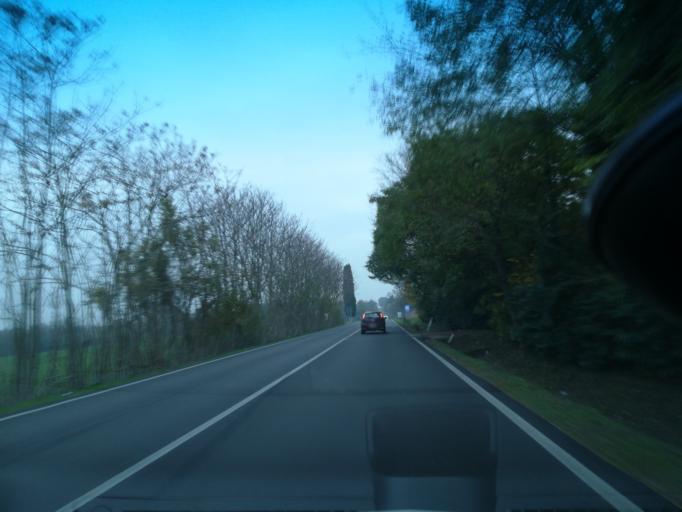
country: IT
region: Emilia-Romagna
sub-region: Provincia di Bologna
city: Imola
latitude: 44.3409
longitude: 11.7460
